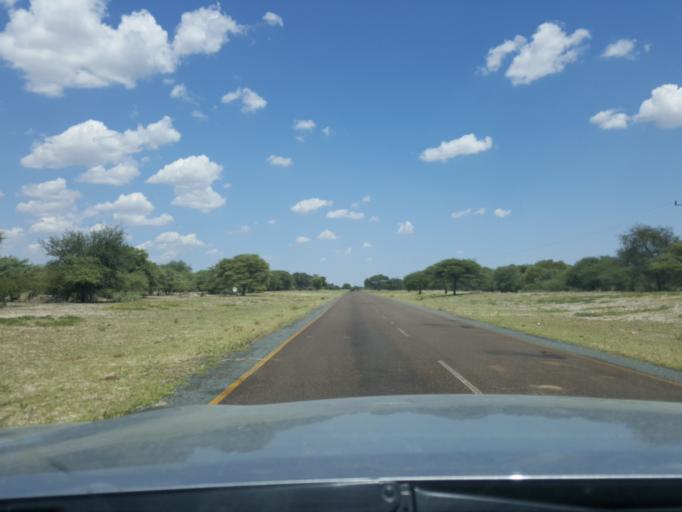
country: BW
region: North West
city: Maun
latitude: -20.1561
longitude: 23.2699
